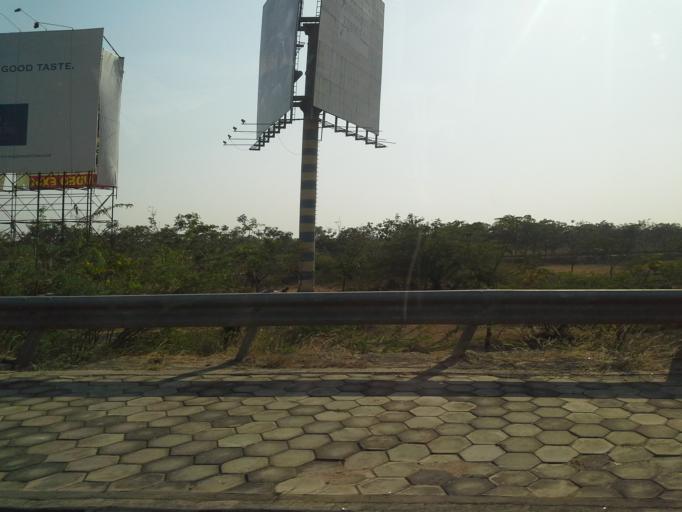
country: IN
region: Telangana
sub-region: Rangareddi
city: Balapur
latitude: 17.2442
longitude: 78.3856
